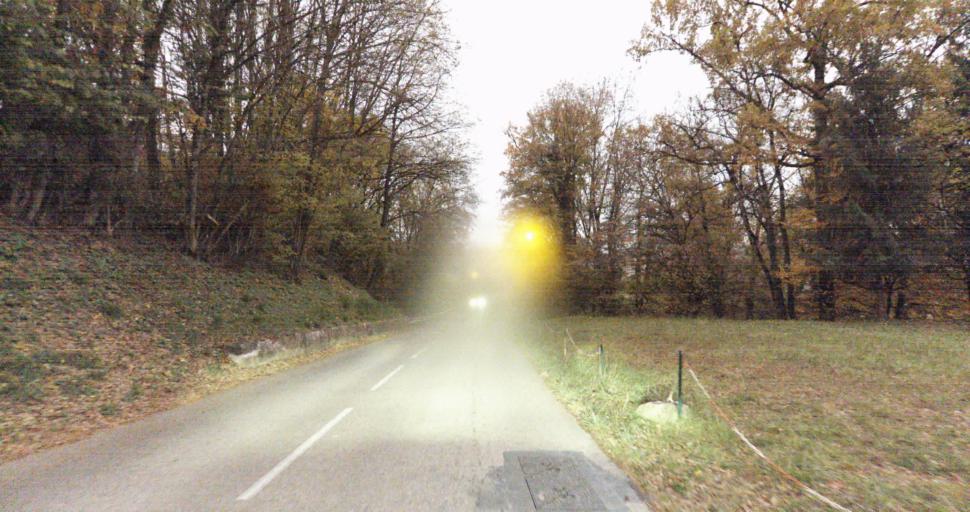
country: FR
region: Rhone-Alpes
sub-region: Departement de la Haute-Savoie
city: Alby-sur-Cheran
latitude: 45.8363
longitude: 6.0095
